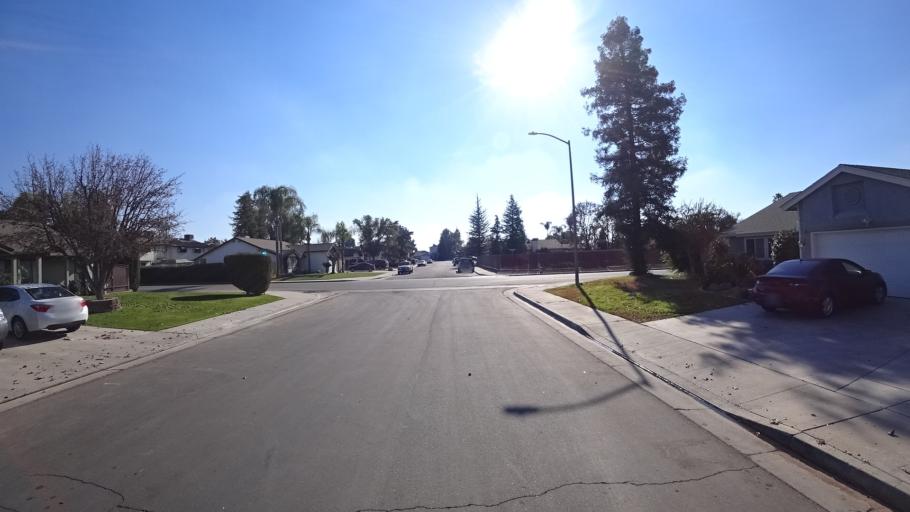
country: US
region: California
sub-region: Kern County
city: Greenfield
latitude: 35.2983
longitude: -119.0431
